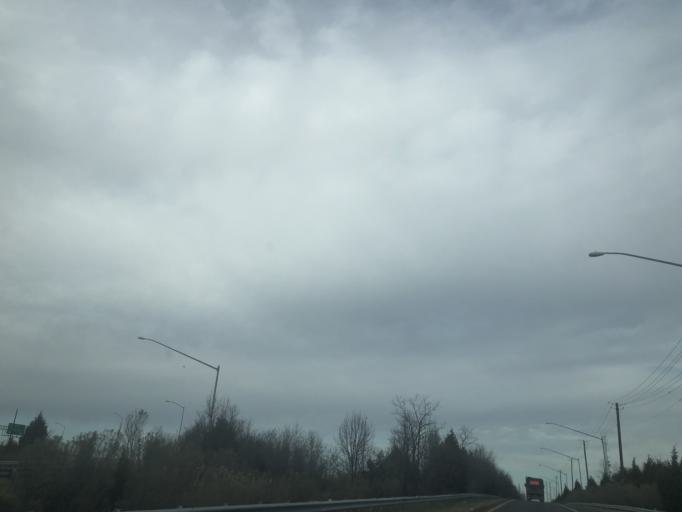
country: US
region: Maryland
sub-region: Prince George's County
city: Oxon Hill
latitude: 38.7983
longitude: -76.9976
